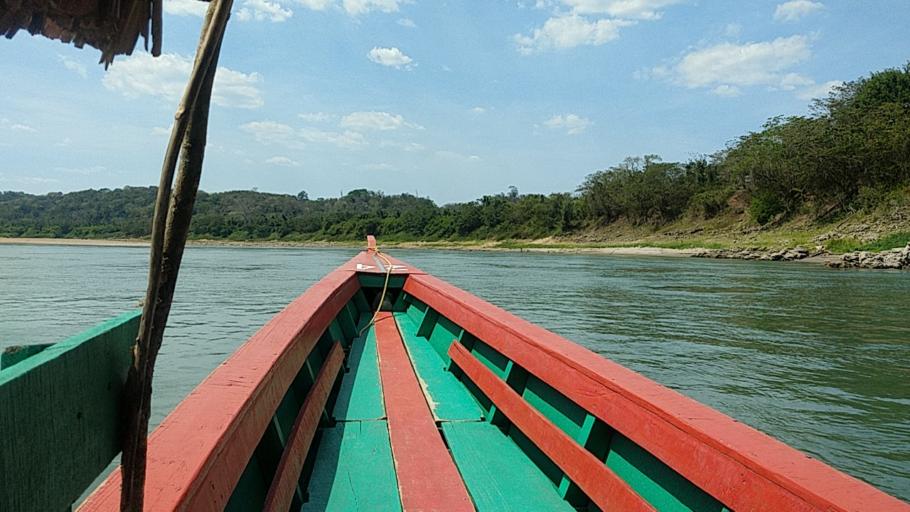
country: MX
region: Chiapas
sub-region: Ocosingo
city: Frontera Corozal
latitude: 16.8935
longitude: -90.9561
